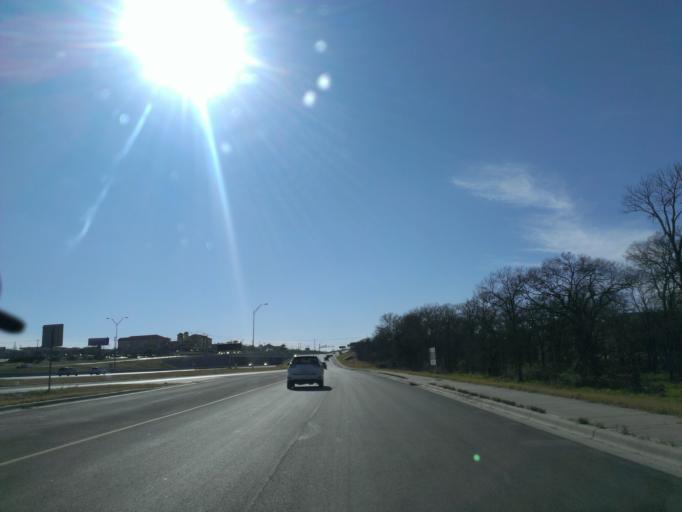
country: US
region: Texas
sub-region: Travis County
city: Austin
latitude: 30.2213
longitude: -97.6867
